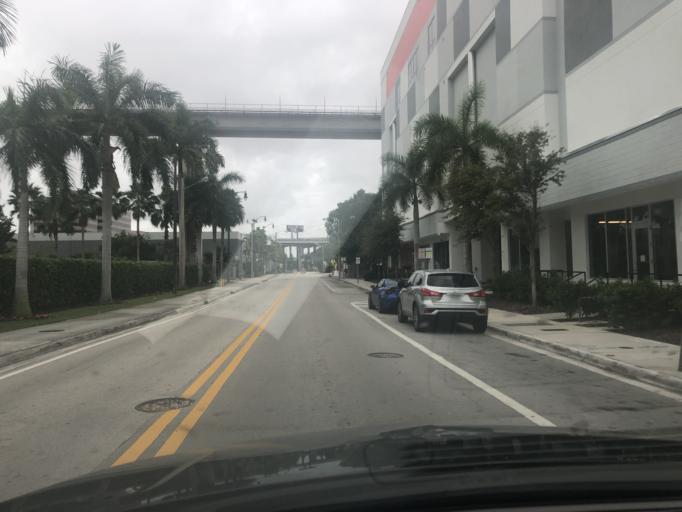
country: US
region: Florida
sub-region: Miami-Dade County
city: Miami
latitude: 25.7712
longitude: -80.1952
